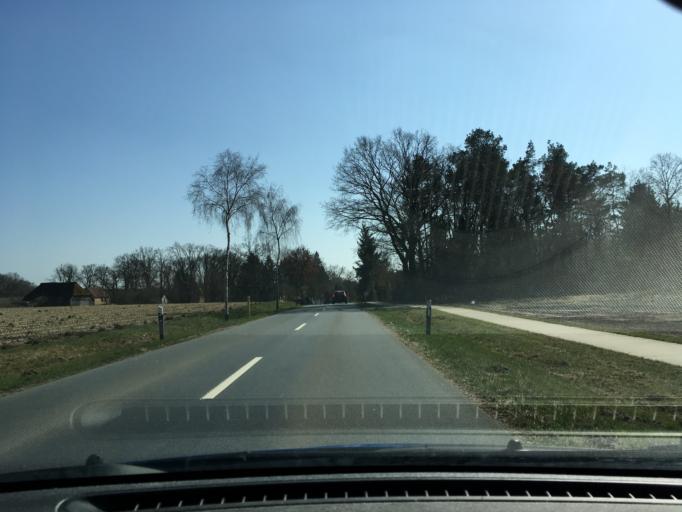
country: DE
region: Lower Saxony
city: Eimke
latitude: 52.9766
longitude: 10.3096
